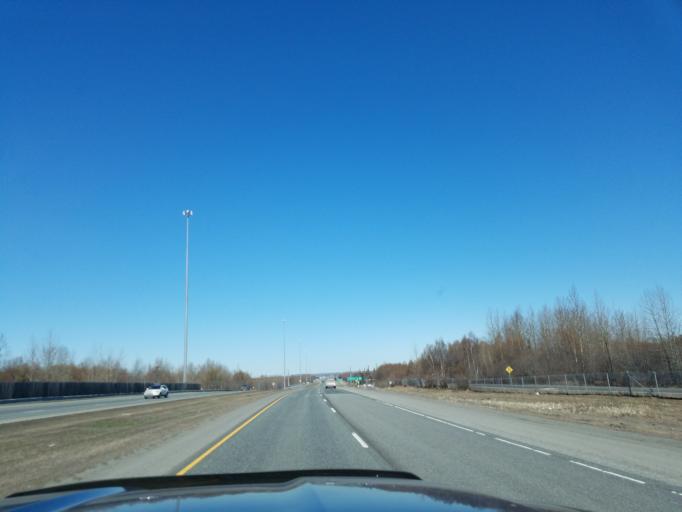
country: US
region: Alaska
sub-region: Anchorage Municipality
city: Anchorage
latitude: 61.1178
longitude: -149.8562
